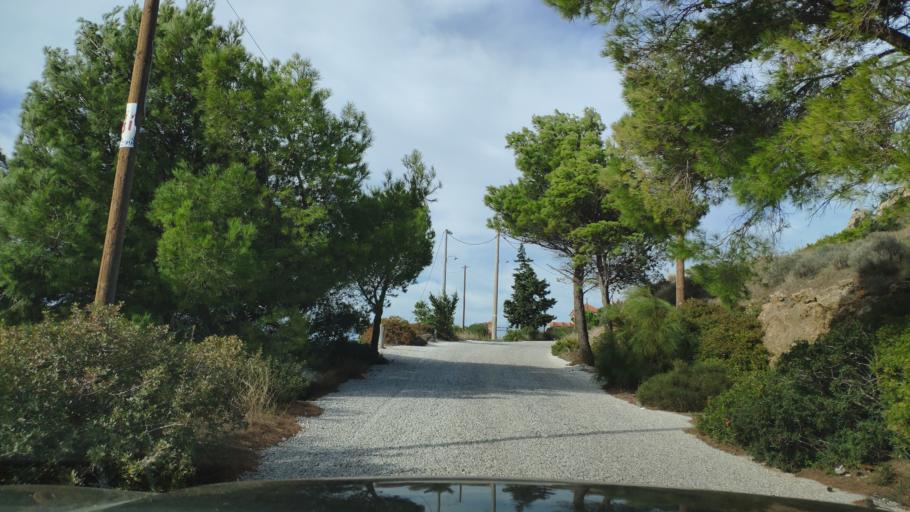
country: GR
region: Attica
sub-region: Nomarchia Anatolikis Attikis
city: Limin Mesoyaias
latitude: 37.9081
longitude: 24.0203
